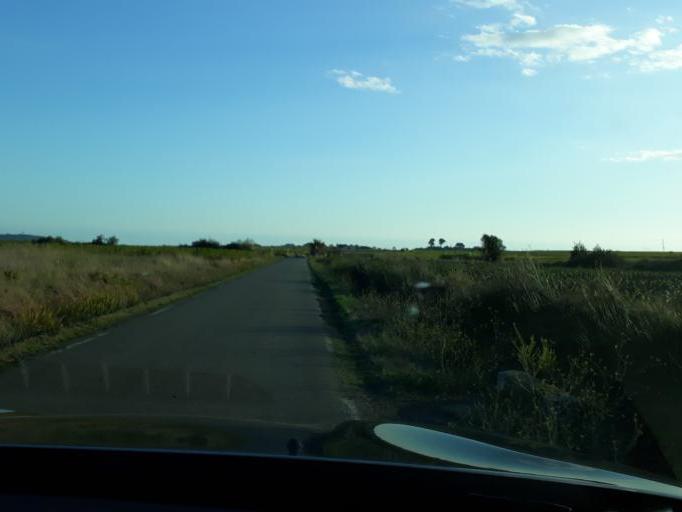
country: FR
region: Languedoc-Roussillon
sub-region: Departement de l'Herault
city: Pomerols
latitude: 43.3628
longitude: 3.4920
